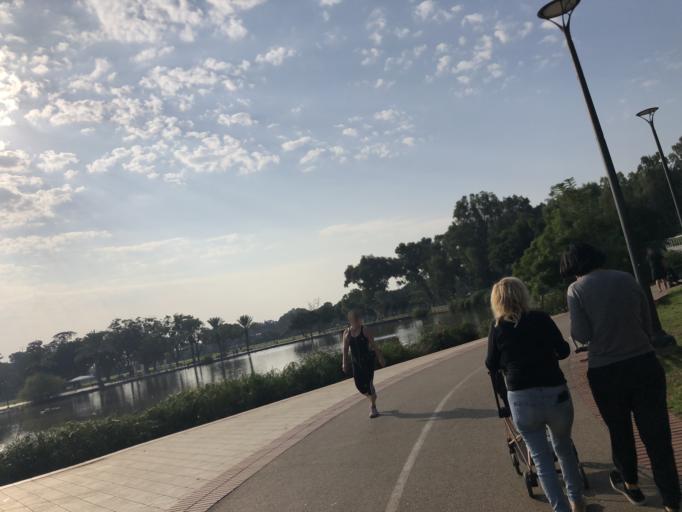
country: IL
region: Tel Aviv
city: Giv`atayim
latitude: 32.0507
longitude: 34.8235
